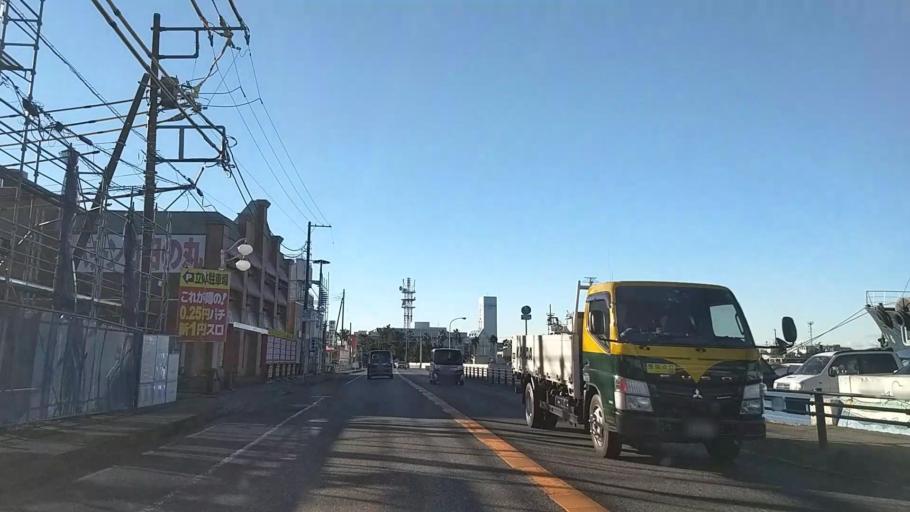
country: JP
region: Chiba
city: Kisarazu
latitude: 35.3839
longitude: 139.9181
